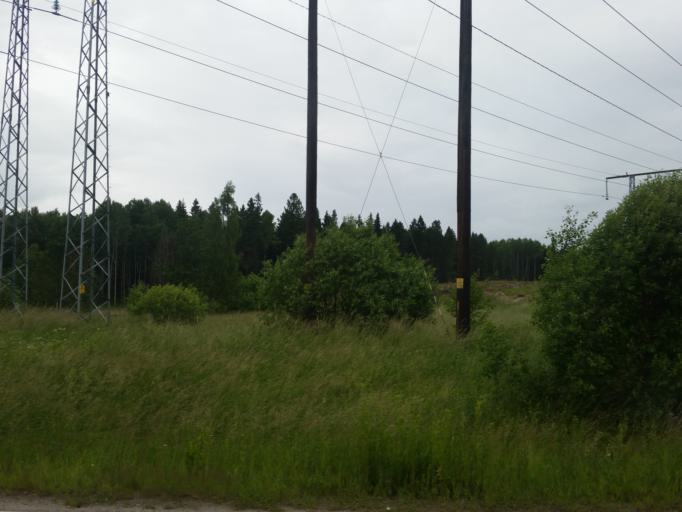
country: SE
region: Stockholm
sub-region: Stockholms Kommun
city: Kista
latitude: 59.4201
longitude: 17.9109
